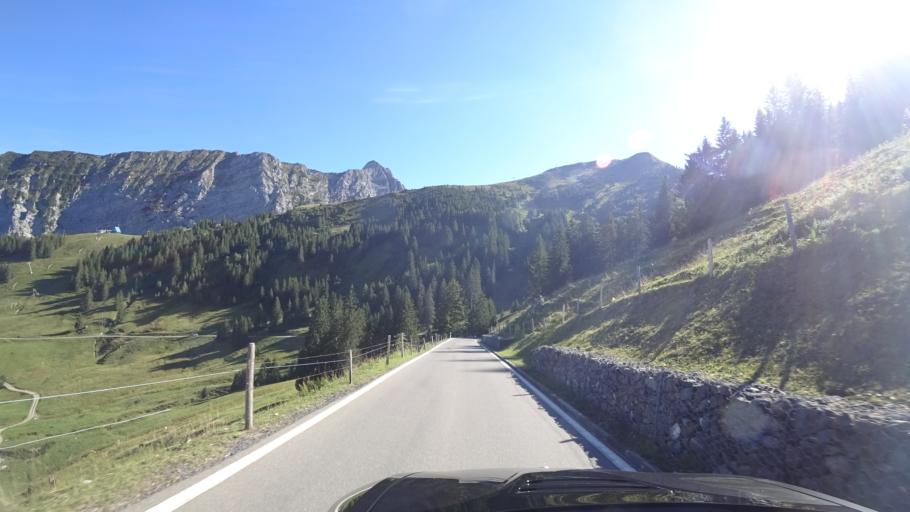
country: CH
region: Obwalden
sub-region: Obwalden
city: Lungern
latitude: 46.8250
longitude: 8.1014
